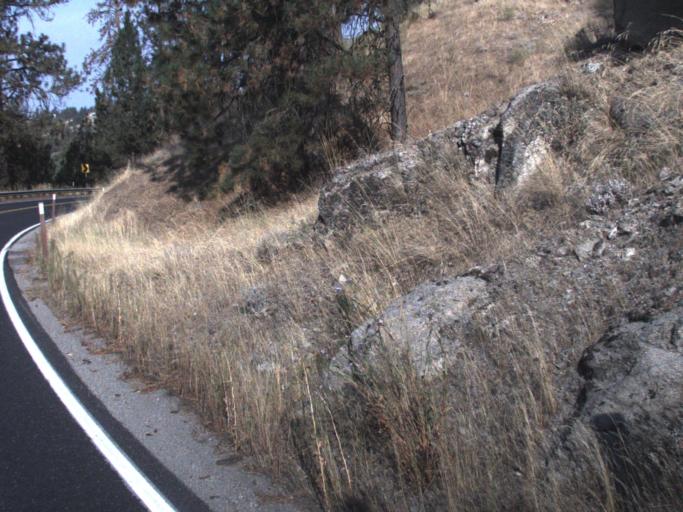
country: US
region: Washington
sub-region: Spokane County
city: Fairwood
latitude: 47.7986
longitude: -117.5377
